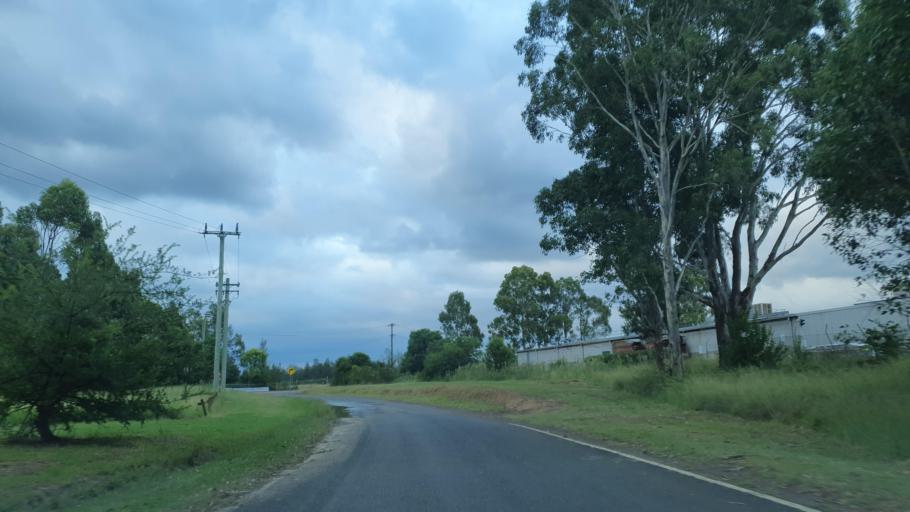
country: AU
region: New South Wales
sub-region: Penrith Municipality
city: Werrington County
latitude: -33.7416
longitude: 150.7628
